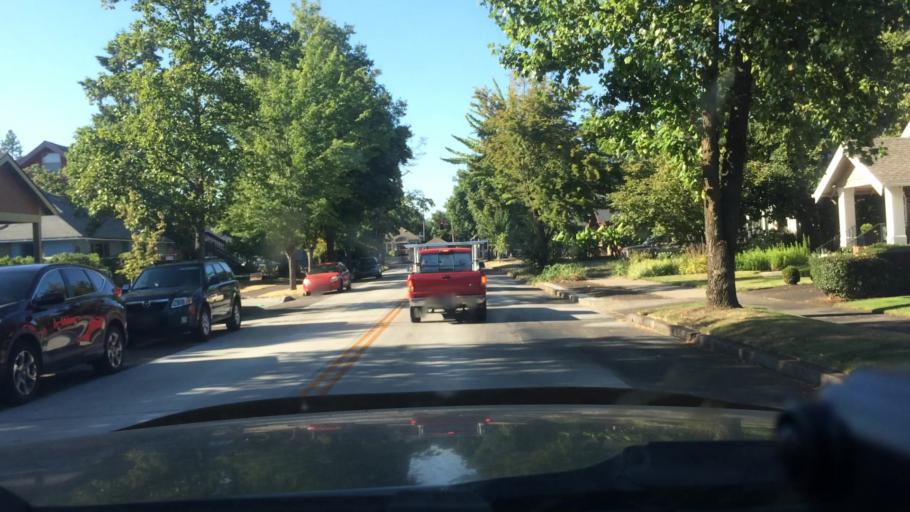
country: US
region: Oregon
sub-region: Lane County
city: Eugene
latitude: 44.0444
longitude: -123.1013
